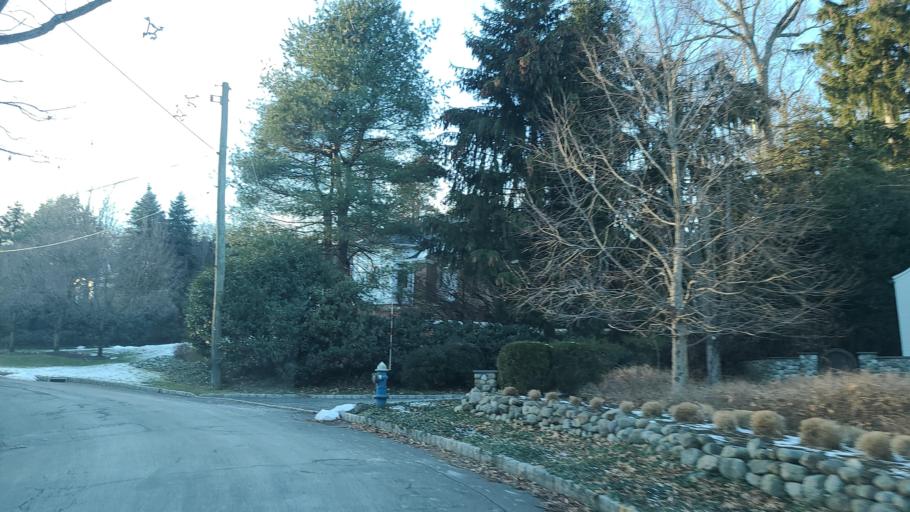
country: US
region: New Jersey
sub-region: Essex County
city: Short Hills
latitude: 40.7299
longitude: -74.3397
